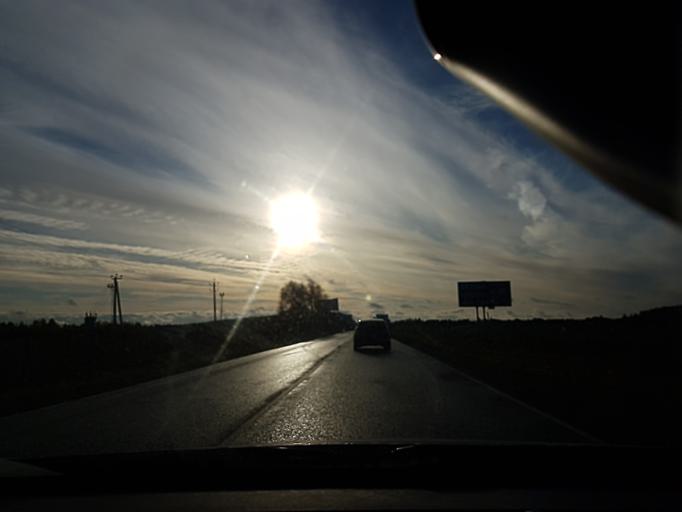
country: RU
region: Moskovskaya
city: Rozhdestveno
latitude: 55.8297
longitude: 37.0324
